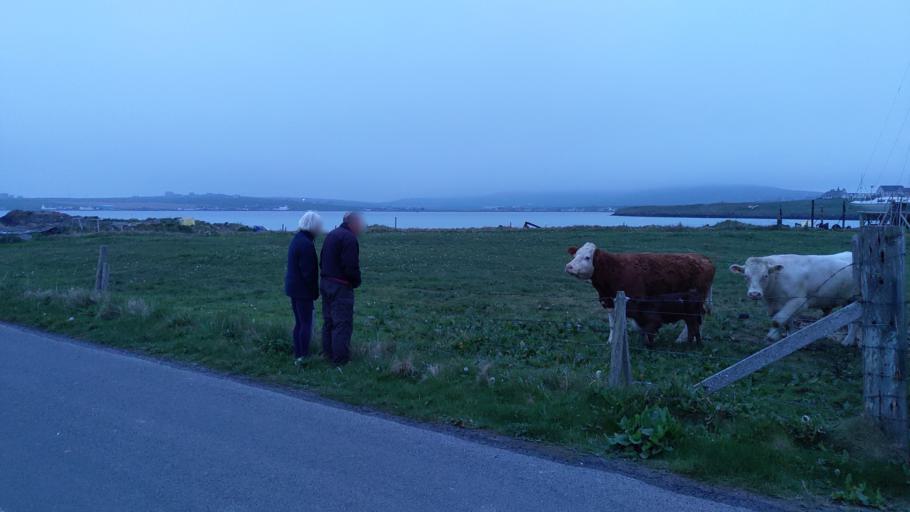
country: GB
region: Scotland
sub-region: Orkney Islands
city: Kirkwall
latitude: 59.3266
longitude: -2.9801
